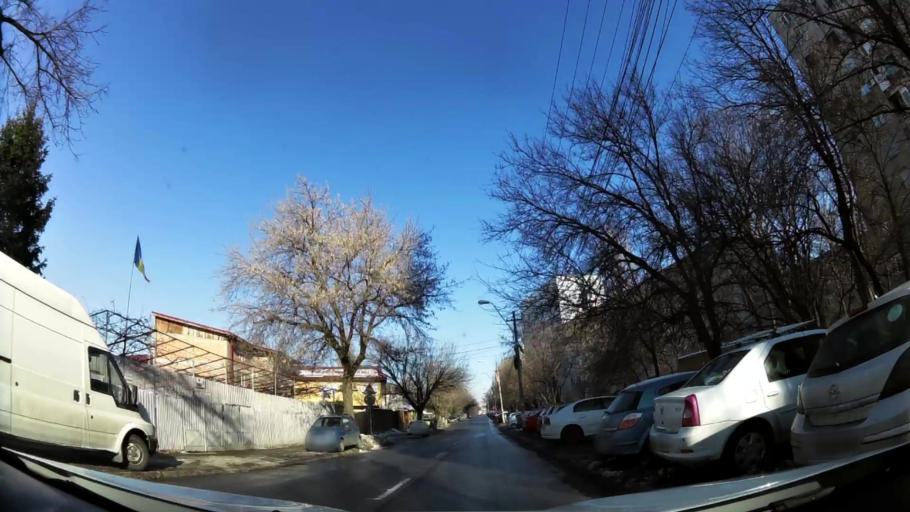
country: RO
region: Bucuresti
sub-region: Municipiul Bucuresti
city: Bucuresti
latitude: 44.3937
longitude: 26.0663
